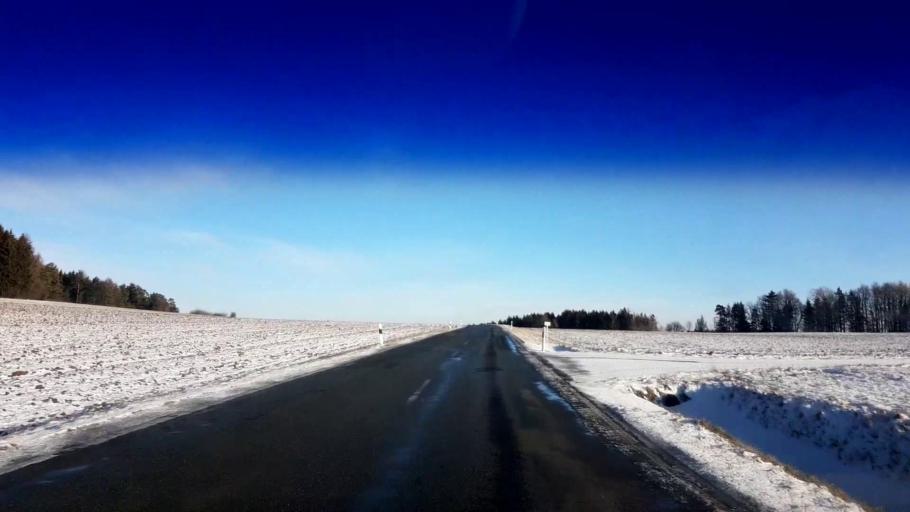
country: DE
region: Bavaria
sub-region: Upper Franconia
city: Heiligenstadt
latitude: 49.8492
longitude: 11.1321
